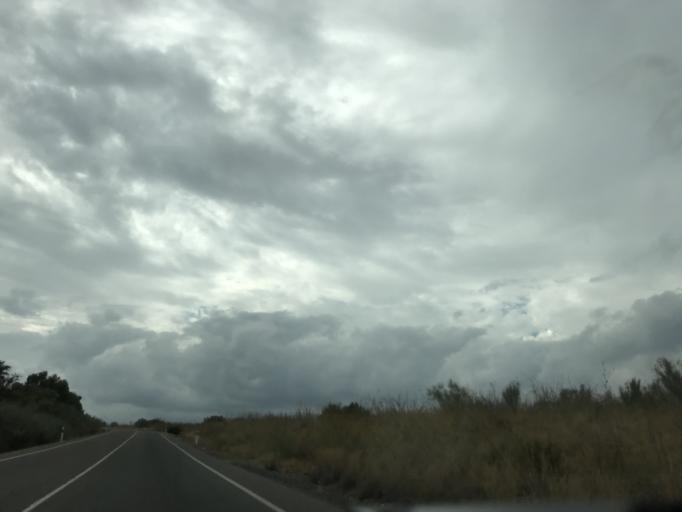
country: ES
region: Andalusia
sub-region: Provincia de Sevilla
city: Tocina
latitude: 37.6403
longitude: -5.7493
